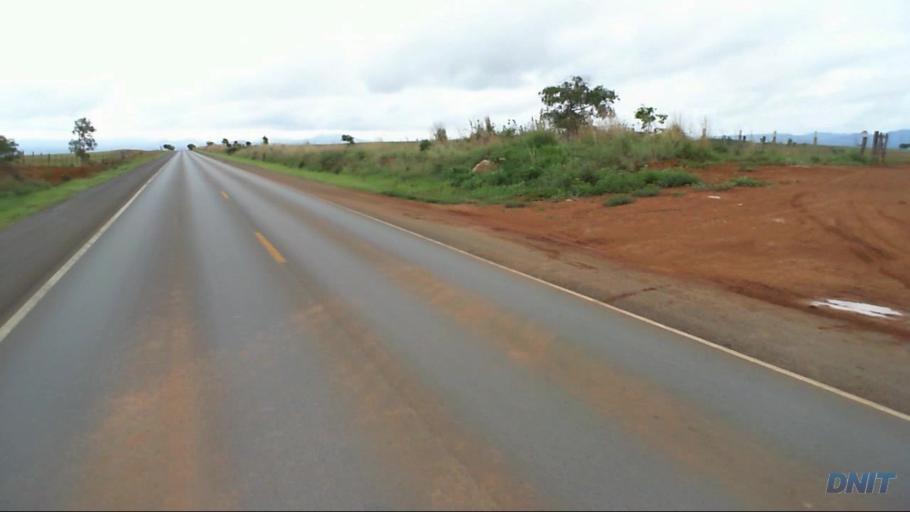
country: BR
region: Goias
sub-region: Padre Bernardo
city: Padre Bernardo
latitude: -15.2115
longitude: -48.4893
